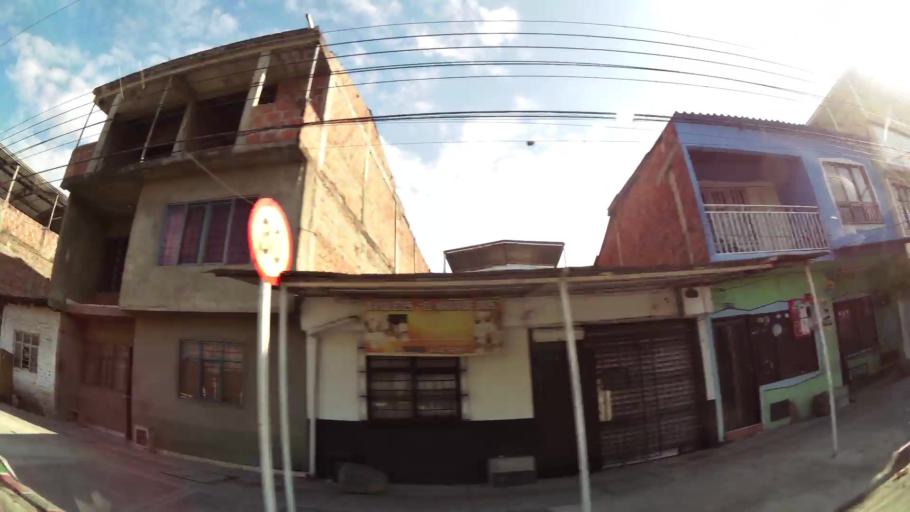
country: CO
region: Valle del Cauca
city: Cali
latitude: 3.4263
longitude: -76.5058
